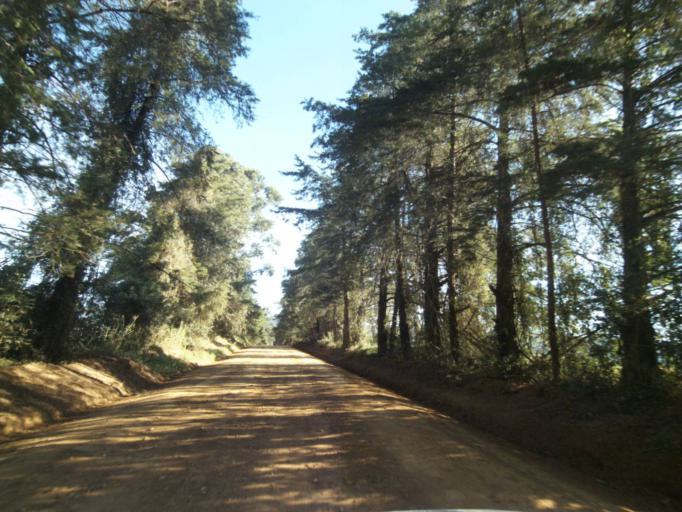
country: BR
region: Parana
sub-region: Tibagi
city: Tibagi
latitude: -24.5286
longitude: -50.5123
